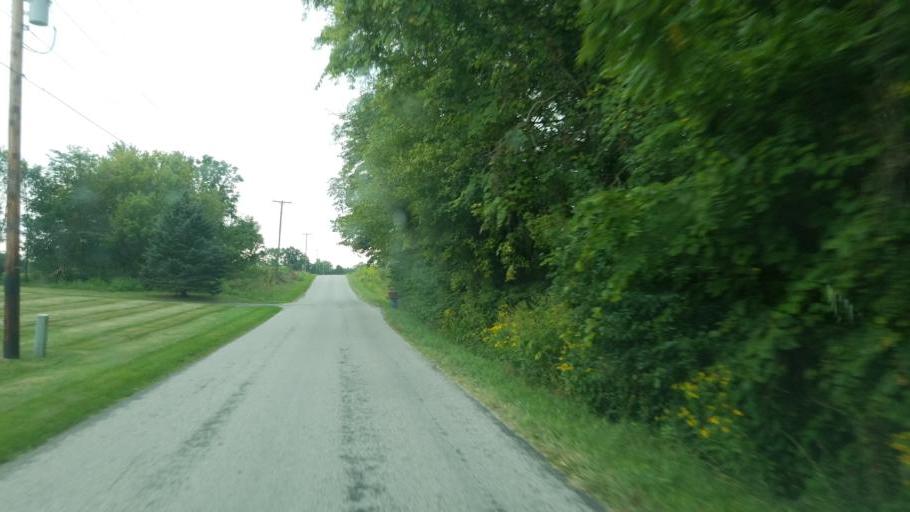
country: US
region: Ohio
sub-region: Crawford County
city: Galion
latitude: 40.7274
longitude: -82.8491
